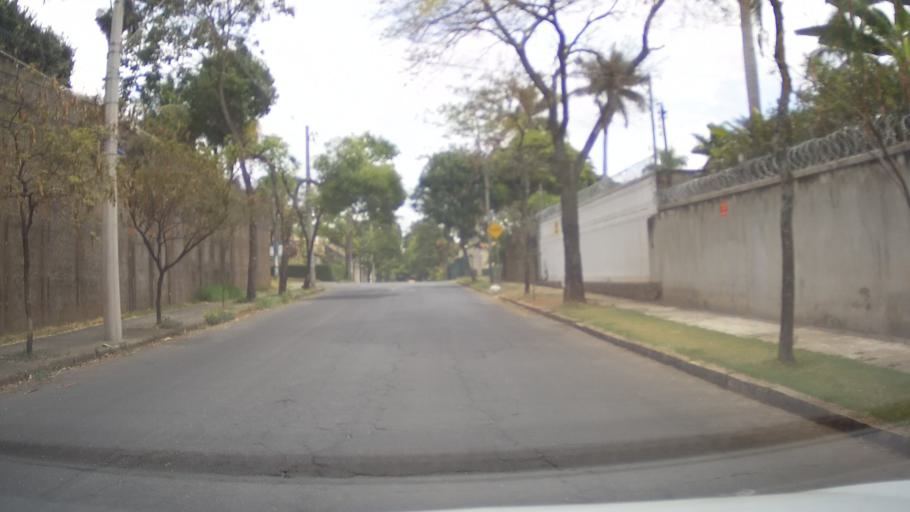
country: BR
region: Minas Gerais
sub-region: Belo Horizonte
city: Belo Horizonte
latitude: -19.8562
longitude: -43.9715
